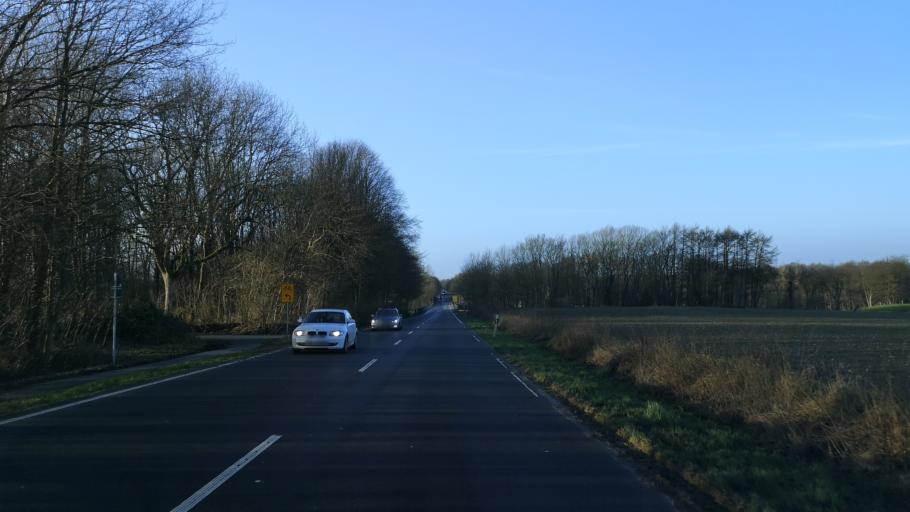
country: DE
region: Schleswig-Holstein
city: Tarp
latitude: 54.6659
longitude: 9.4159
